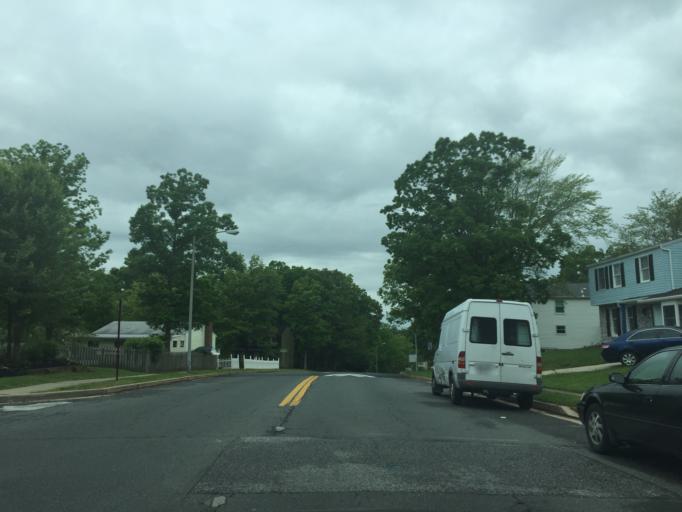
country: US
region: Maryland
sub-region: Baltimore County
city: Perry Hall
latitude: 39.3843
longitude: -76.4641
